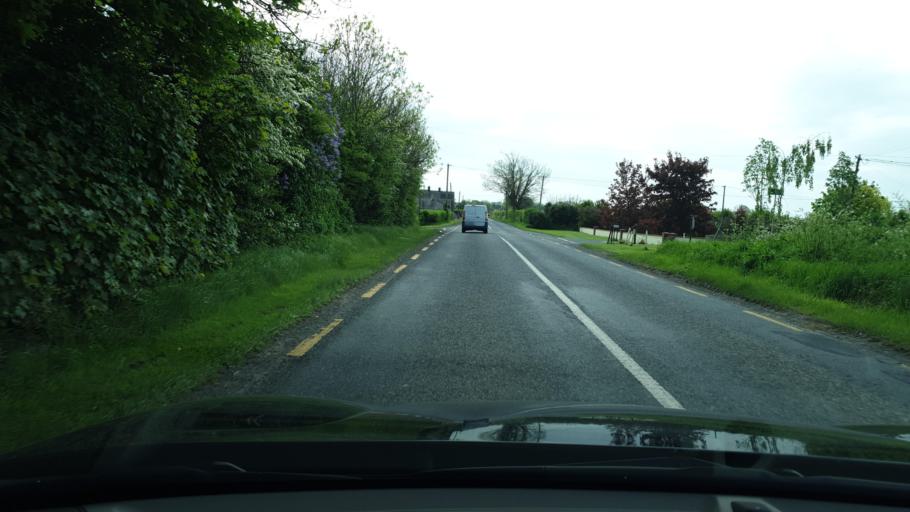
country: IE
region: Leinster
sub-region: An Mhi
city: Navan
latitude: 53.7432
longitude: -6.7161
